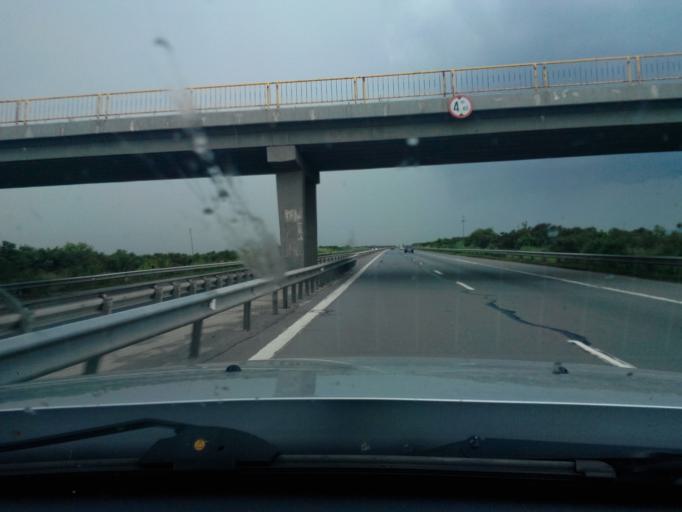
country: RO
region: Arges
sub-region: Comuna Ratesti
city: Ratesti
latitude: 44.7363
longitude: 25.1114
